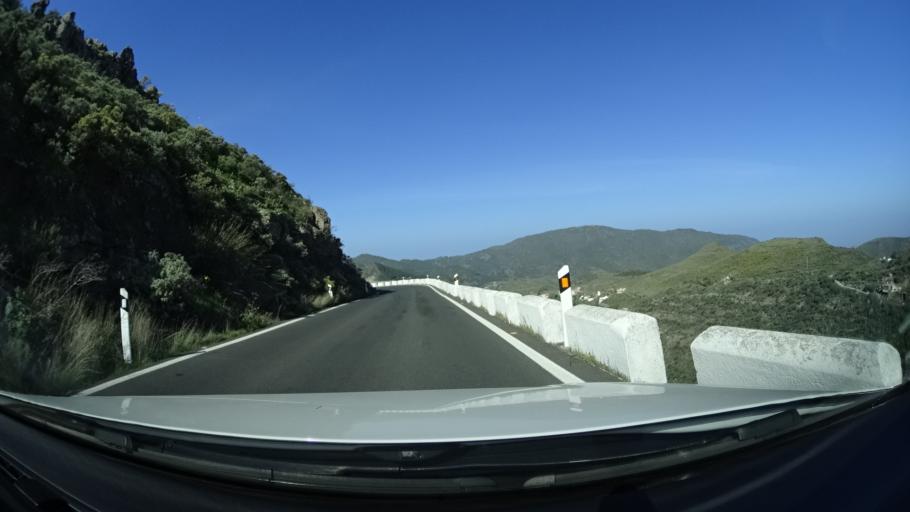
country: ES
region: Canary Islands
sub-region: Provincia de Las Palmas
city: Artenara
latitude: 28.0255
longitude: -15.6422
